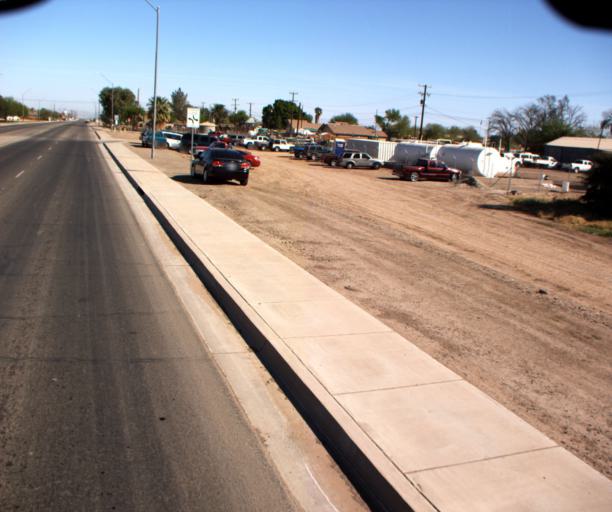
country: US
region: Arizona
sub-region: Yuma County
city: San Luis
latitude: 32.5531
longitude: -114.7847
